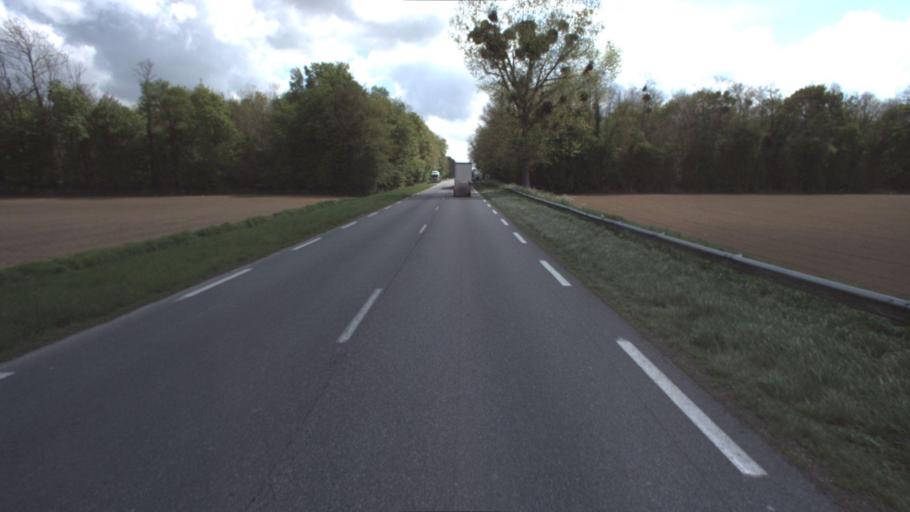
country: FR
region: Ile-de-France
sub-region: Departement de Seine-et-Marne
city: La Ferte-Gaucher
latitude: 48.6935
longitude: 3.3186
